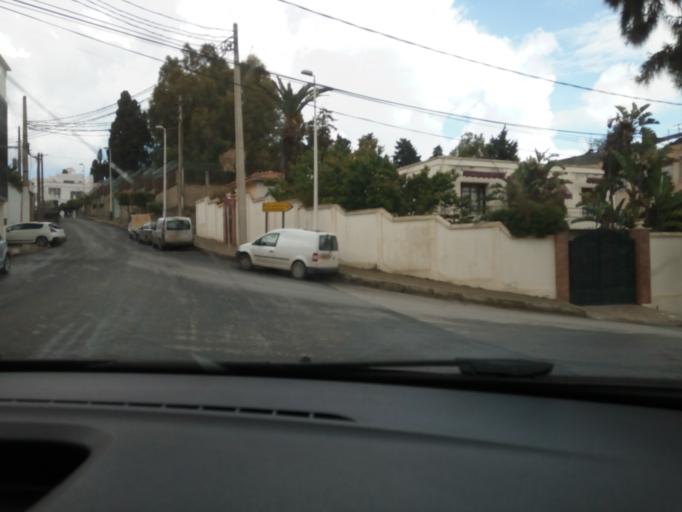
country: DZ
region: Alger
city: Algiers
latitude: 36.7519
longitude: 3.0252
